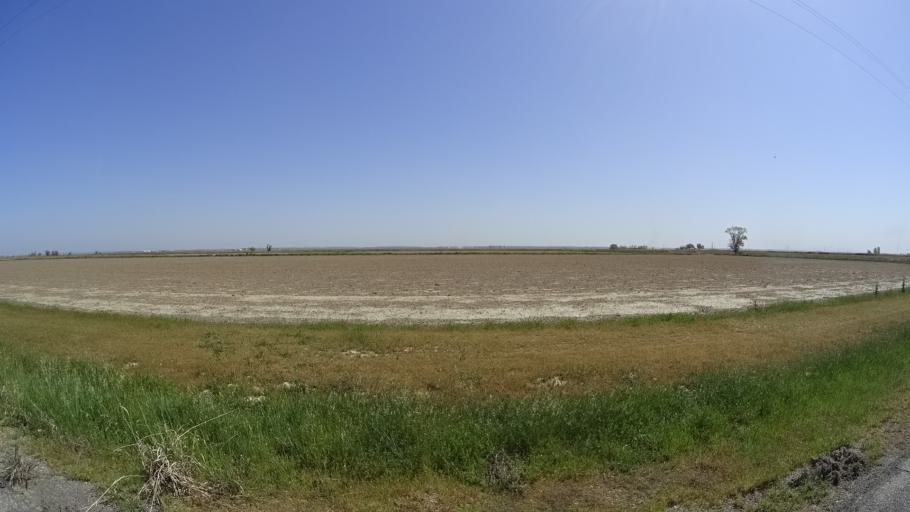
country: US
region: California
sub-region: Glenn County
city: Willows
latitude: 39.4978
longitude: -122.0934
